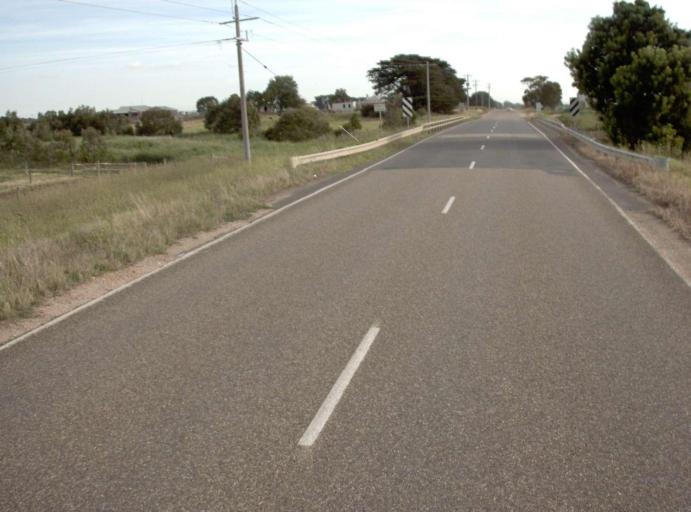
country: AU
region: Victoria
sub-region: Wellington
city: Heyfield
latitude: -37.9817
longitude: 146.8880
